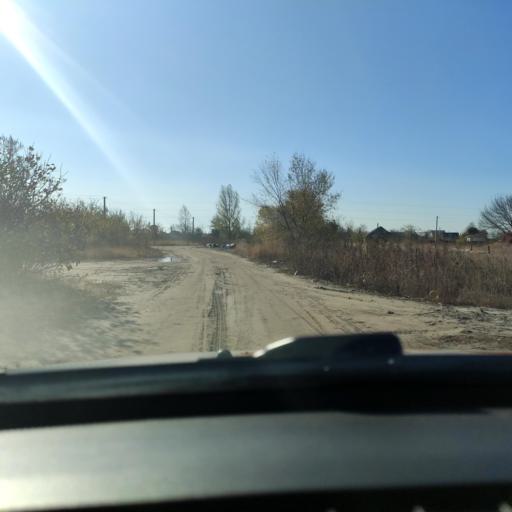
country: RU
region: Voronezj
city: Shilovo
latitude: 51.5203
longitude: 39.1540
